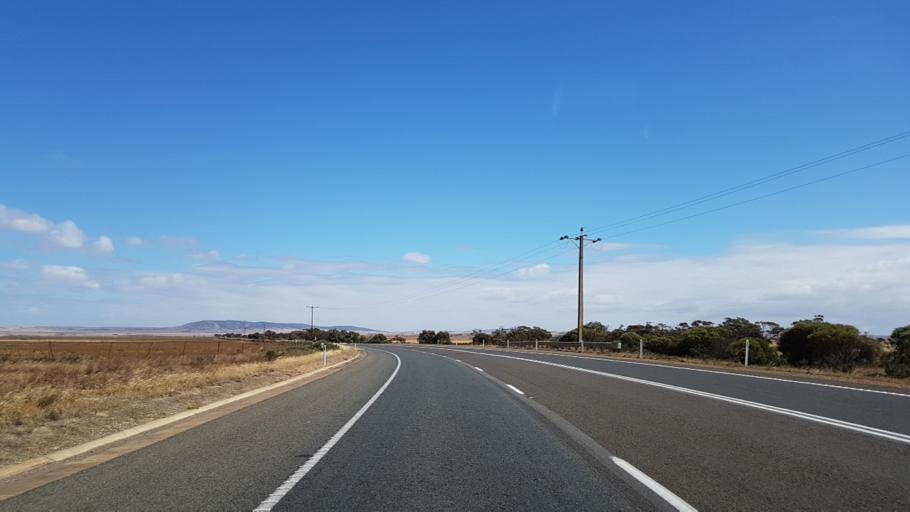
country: AU
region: South Australia
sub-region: Wakefield
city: Balaklava
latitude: -34.1515
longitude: 138.1564
